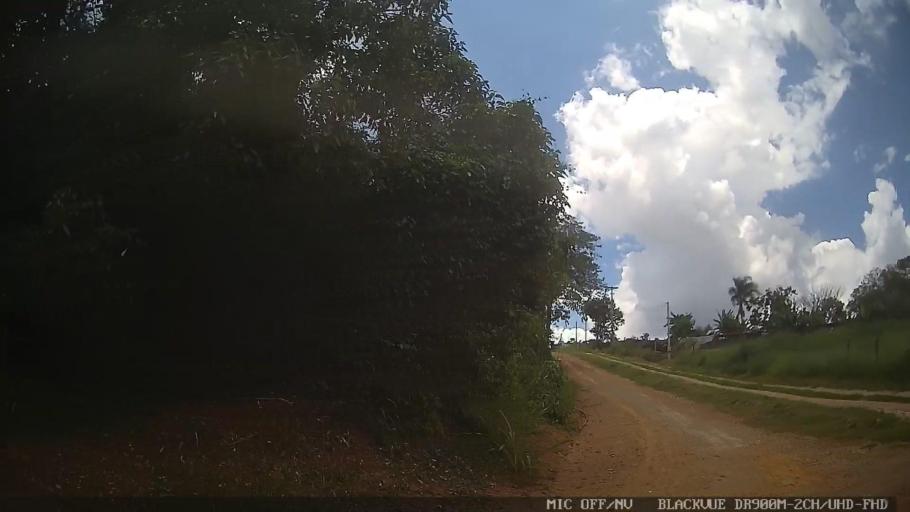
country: BR
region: Sao Paulo
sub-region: Atibaia
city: Atibaia
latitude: -23.1301
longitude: -46.6341
